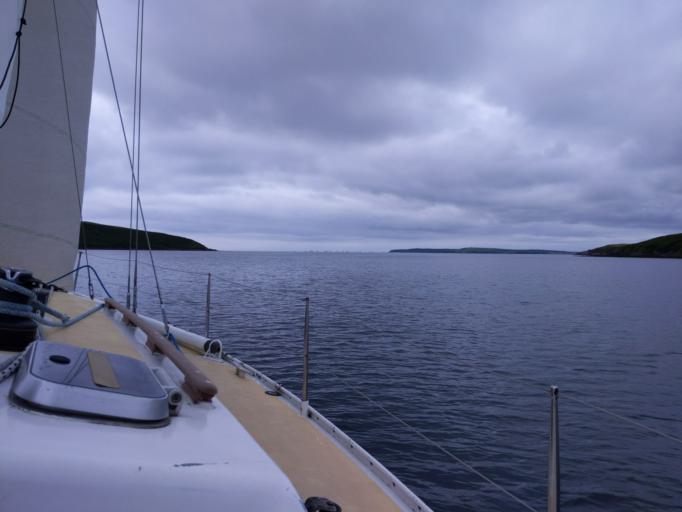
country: IE
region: Munster
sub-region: County Cork
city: Kinsale
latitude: 51.6887
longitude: -8.4988
